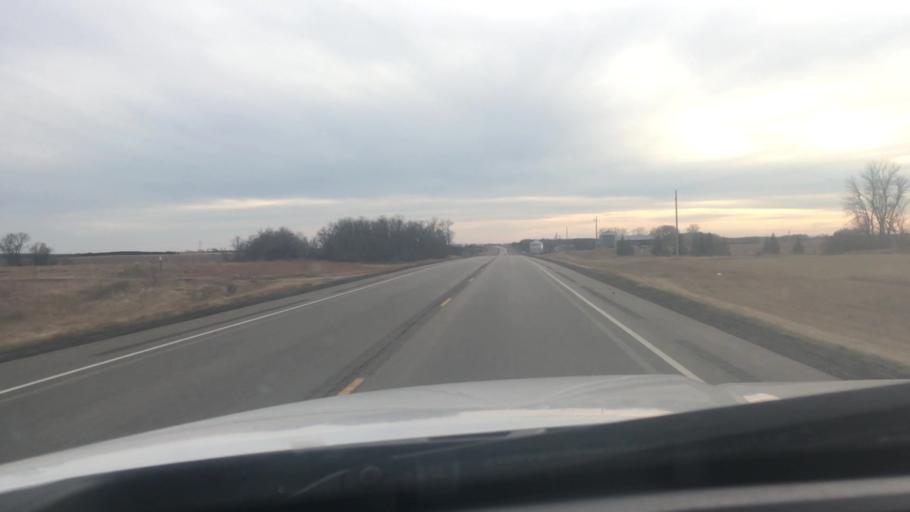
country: US
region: Minnesota
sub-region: Otter Tail County
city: Perham
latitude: 46.3279
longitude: -95.7185
